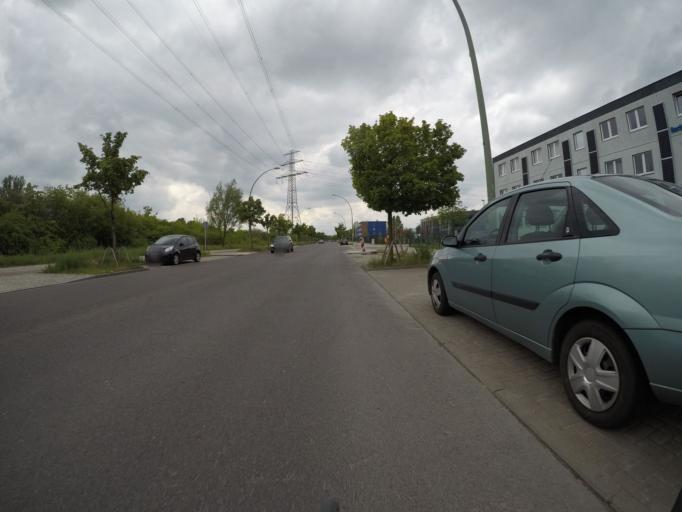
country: DE
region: Berlin
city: Falkenberg
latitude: 52.5520
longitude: 13.5376
